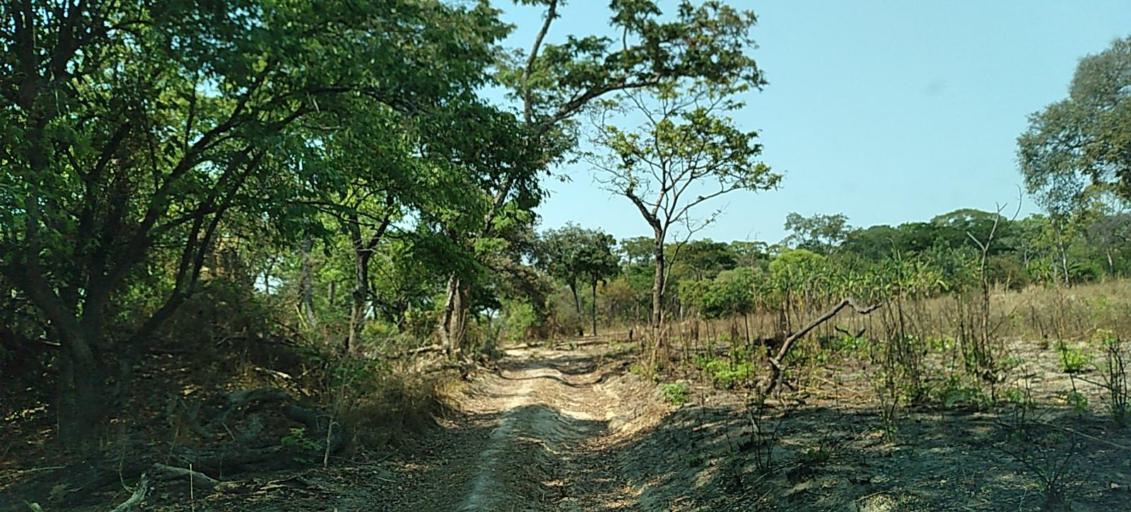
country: ZM
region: Copperbelt
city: Mpongwe
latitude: -13.7881
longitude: 28.0985
